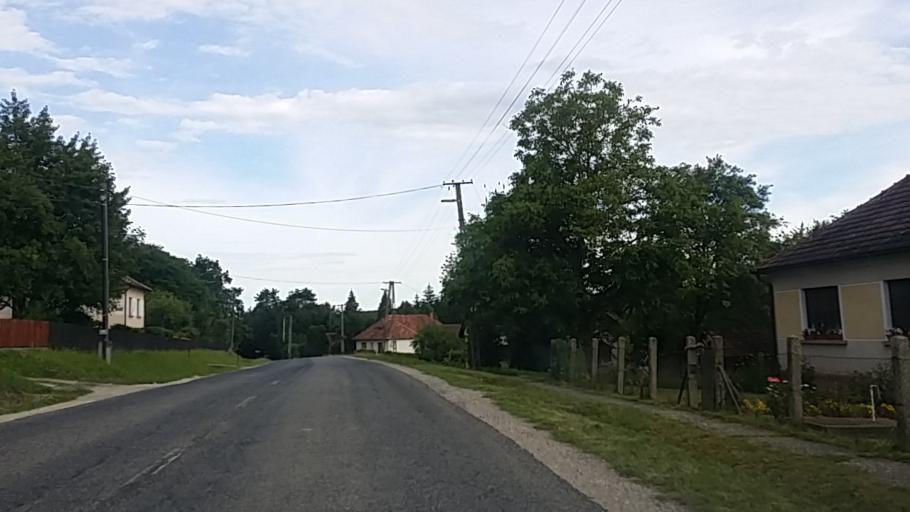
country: SI
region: Hodos-Hodos
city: Hodos
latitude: 46.8298
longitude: 16.4535
